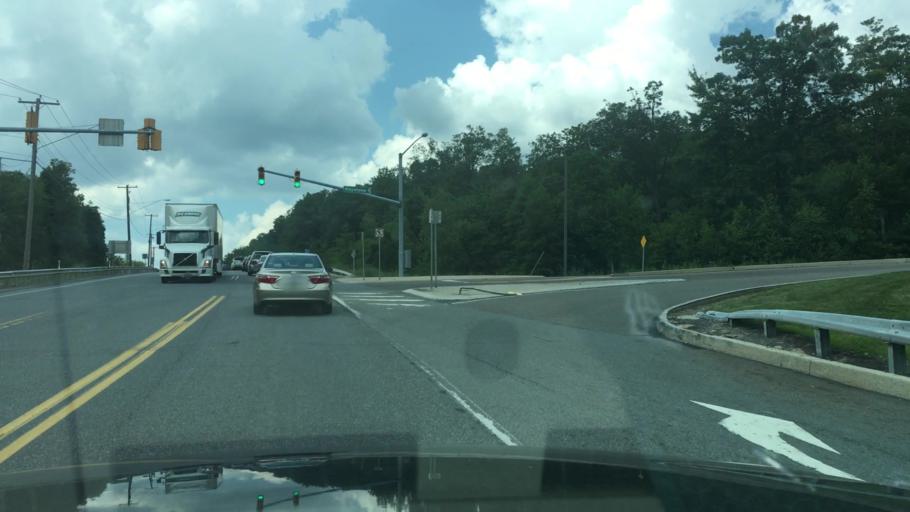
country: US
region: Pennsylvania
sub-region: Schuylkill County
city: Ashland
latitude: 40.7140
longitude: -76.3409
